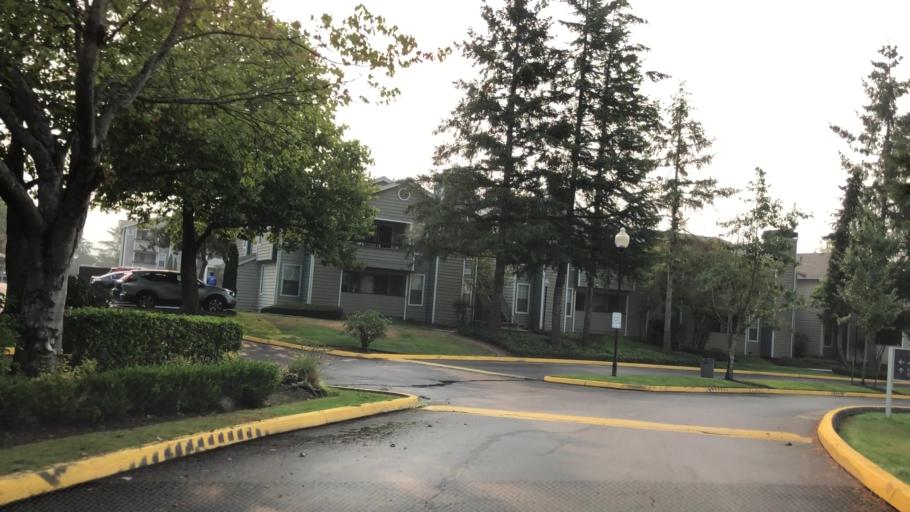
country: US
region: Washington
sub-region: King County
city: Sammamish
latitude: 47.6618
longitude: -122.0923
